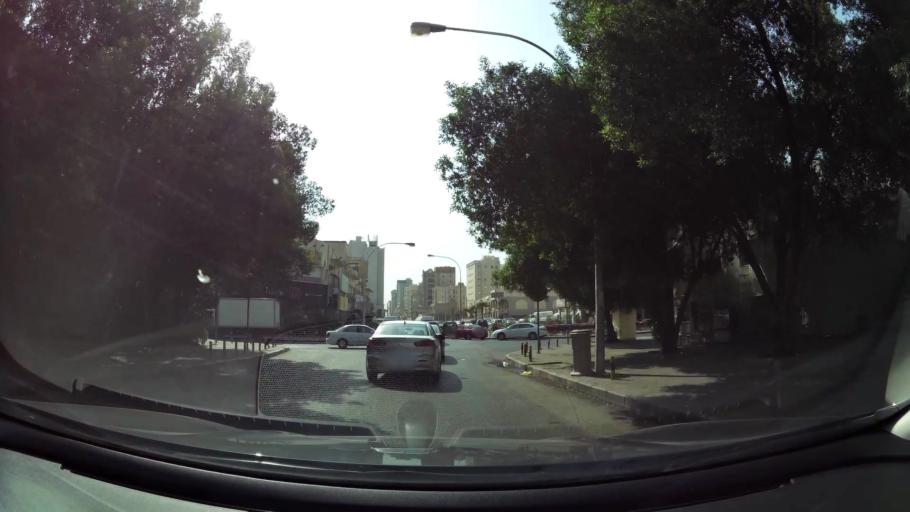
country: KW
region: Muhafazat Hawalli
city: Hawalli
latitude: 29.3333
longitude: 48.0179
